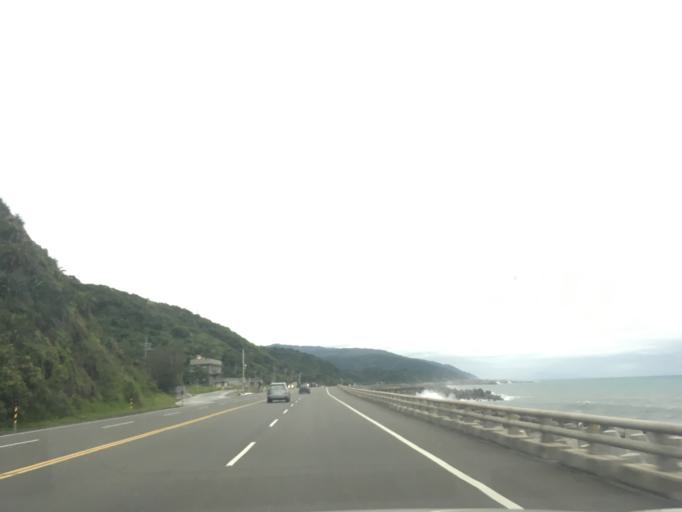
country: TW
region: Taiwan
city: Hengchun
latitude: 22.3218
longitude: 120.8918
